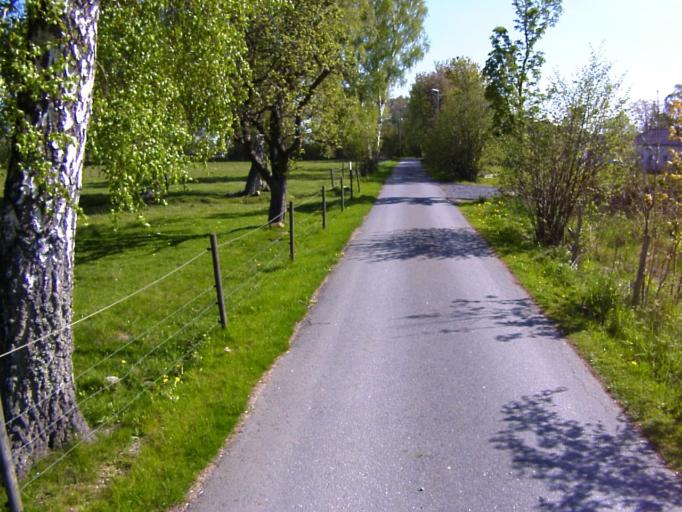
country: SE
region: Skane
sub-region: Kristianstads Kommun
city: Onnestad
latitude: 55.9377
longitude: 13.9649
